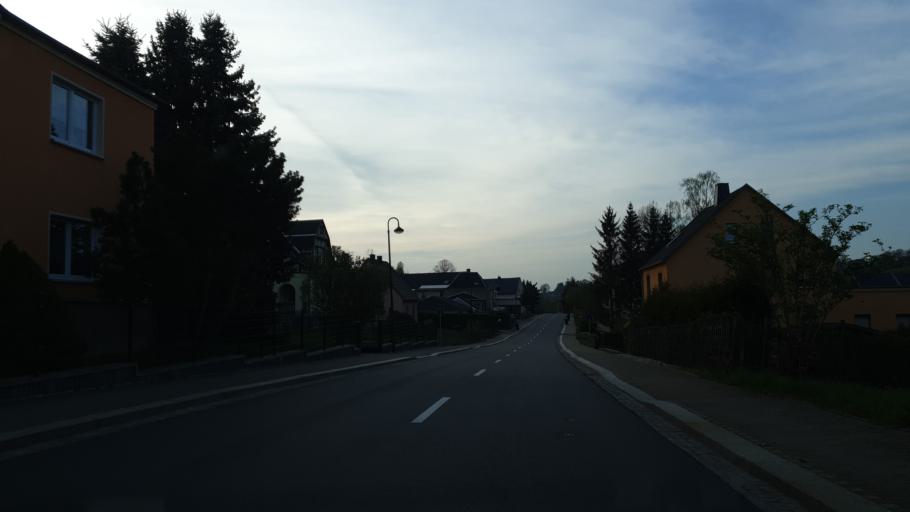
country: DE
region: Saxony
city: Gersdorf
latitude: 50.7427
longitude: 12.7284
